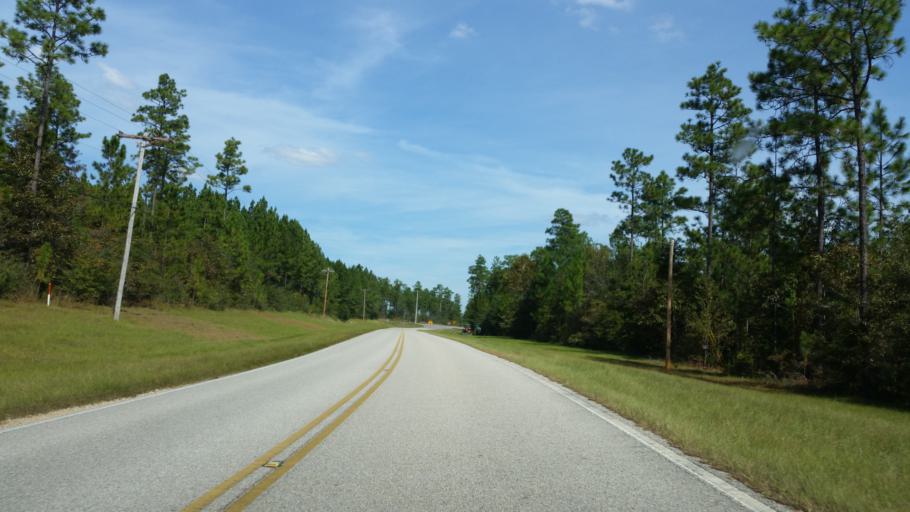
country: US
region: Alabama
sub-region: Baldwin County
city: Spanish Fort
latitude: 30.7300
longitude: -87.8367
